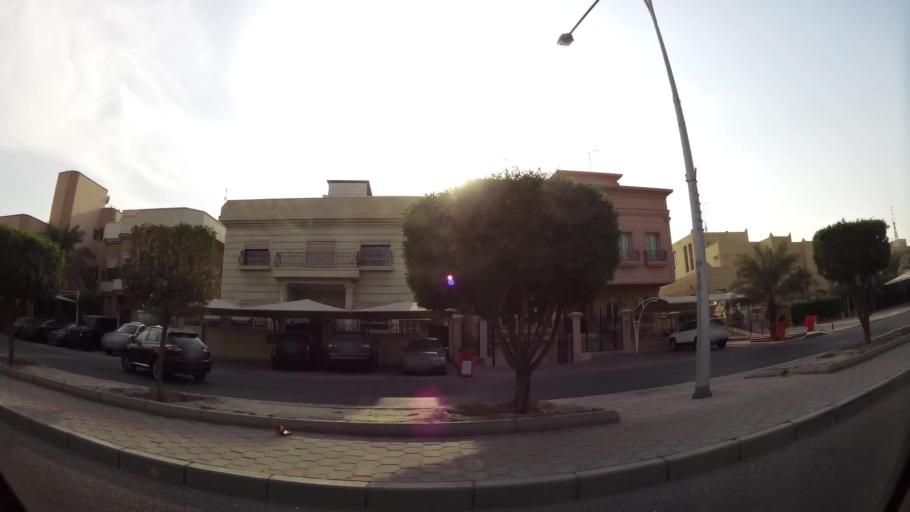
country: KW
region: Muhafazat Hawalli
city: Hawalli
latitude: 29.3169
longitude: 48.0020
